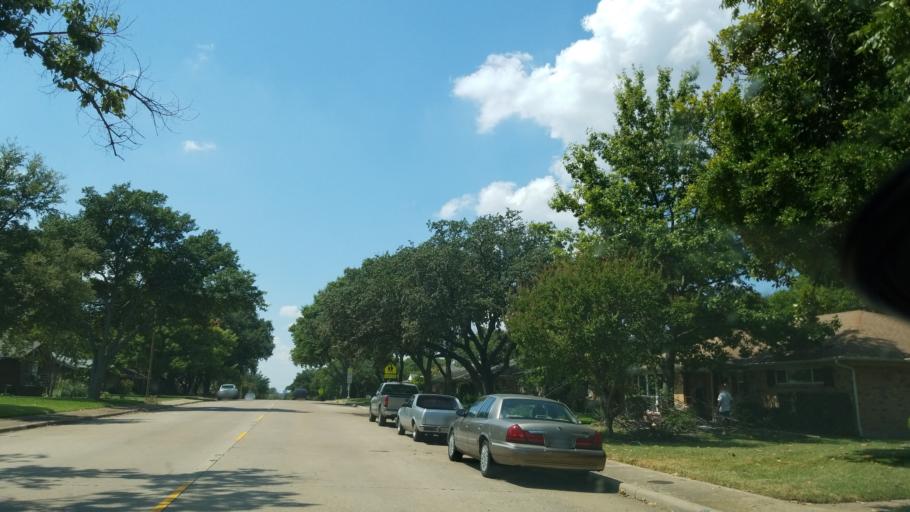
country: US
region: Texas
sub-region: Dallas County
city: Richardson
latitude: 32.8862
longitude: -96.7052
